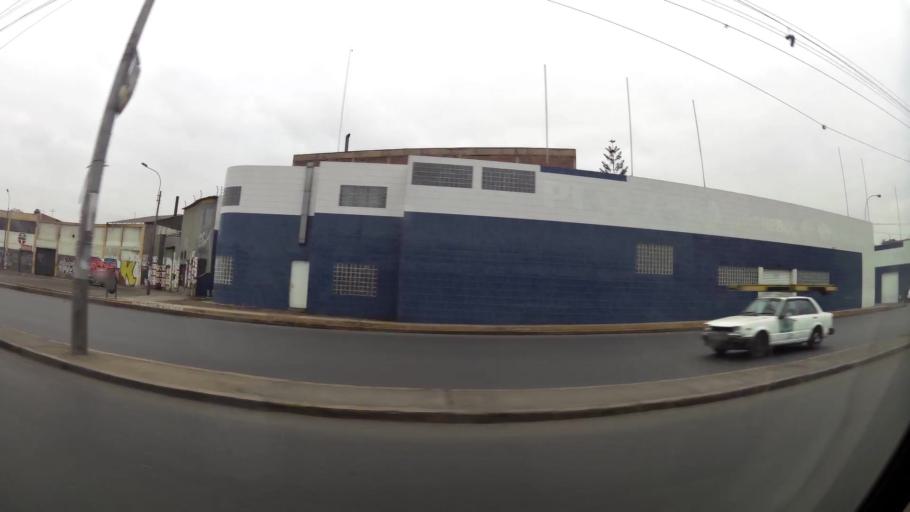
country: PE
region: Lima
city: Lima
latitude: -12.0471
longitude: -77.0524
